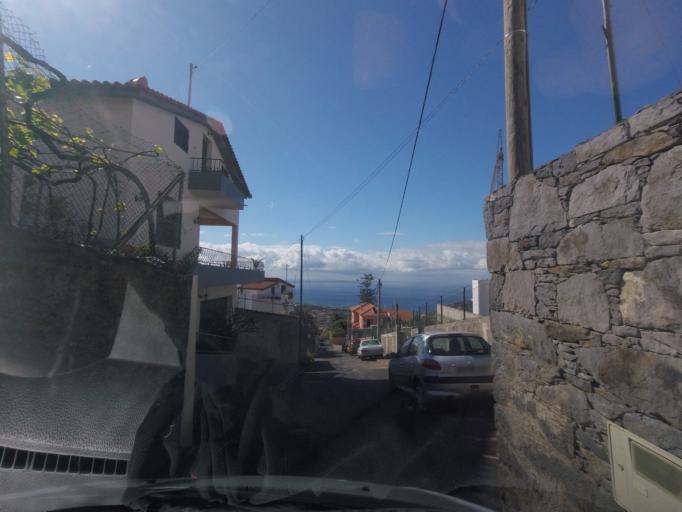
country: PT
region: Madeira
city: Camara de Lobos
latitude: 32.6633
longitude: -16.9748
